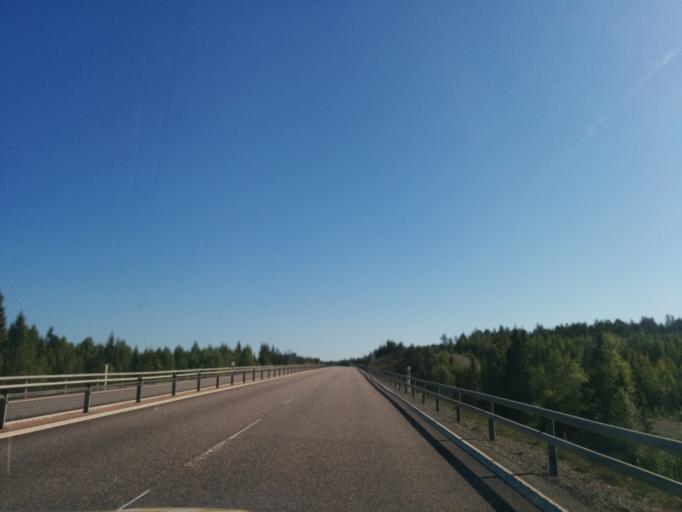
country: SE
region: Vaesternorrland
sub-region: Haernoesands Kommun
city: Haernoesand
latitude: 62.7173
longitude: 17.9117
